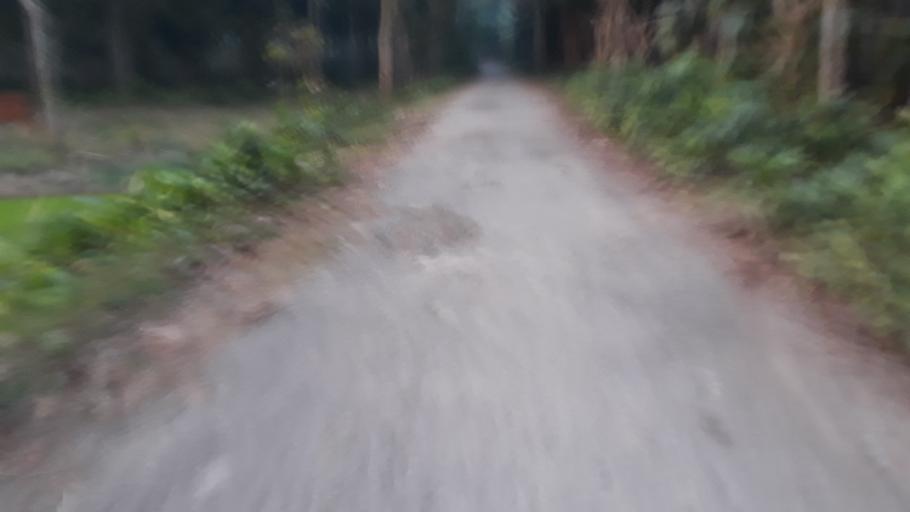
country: BD
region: Khulna
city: Kaliganj
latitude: 23.3484
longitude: 88.9071
